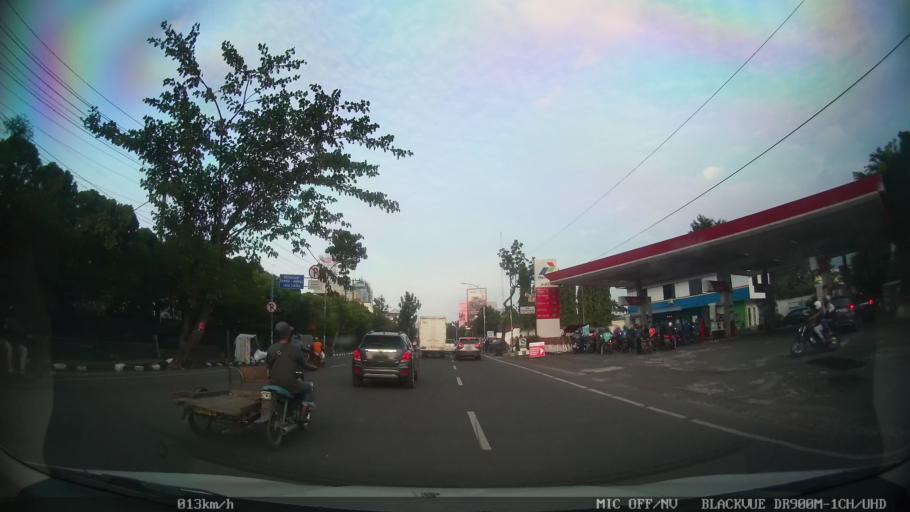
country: ID
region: North Sumatra
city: Medan
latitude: 3.5989
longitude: 98.6839
